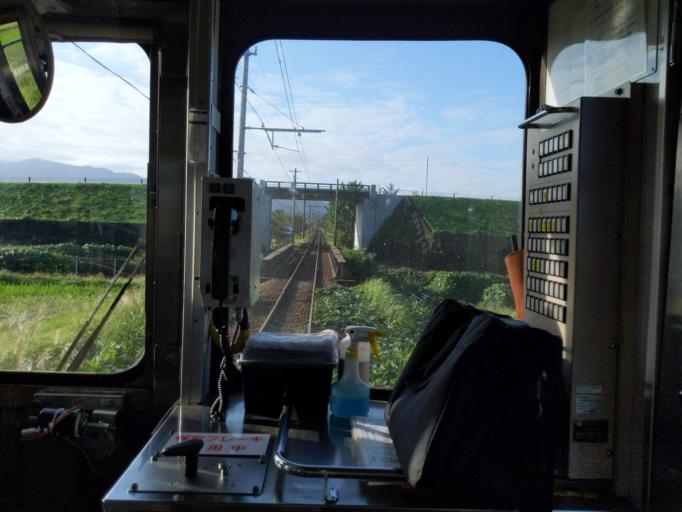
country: JP
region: Toyama
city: Kamiichi
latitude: 36.6120
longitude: 137.3203
